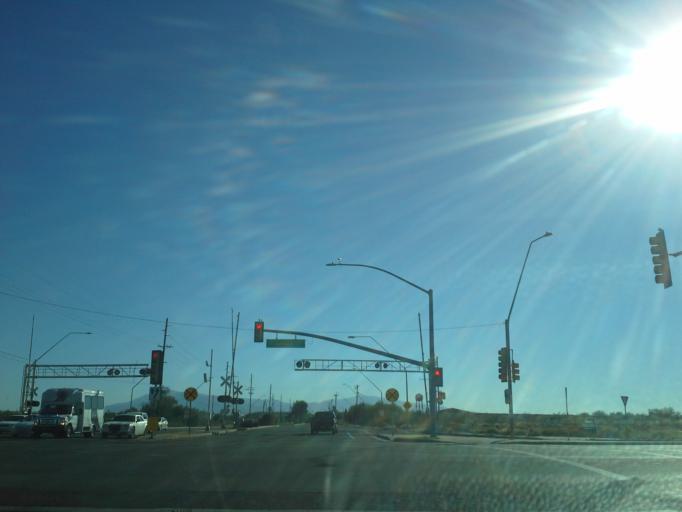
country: US
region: Arizona
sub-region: Pima County
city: South Tucson
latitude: 32.1338
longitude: -110.9619
